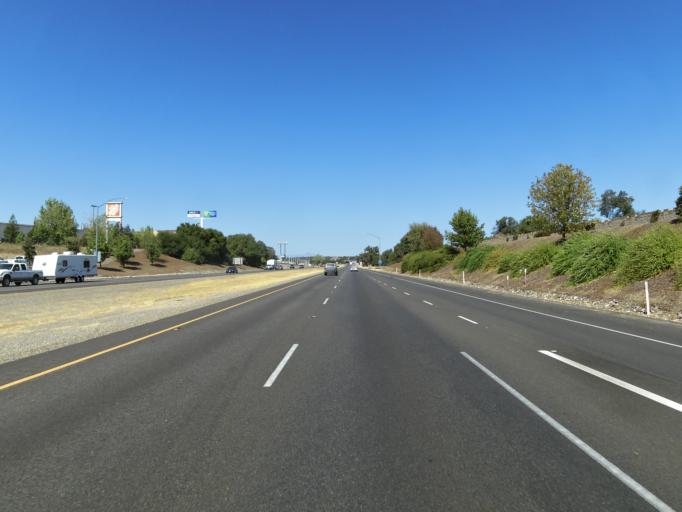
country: US
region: California
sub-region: Tehama County
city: Red Bluff
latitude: 40.1941
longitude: -122.2364
